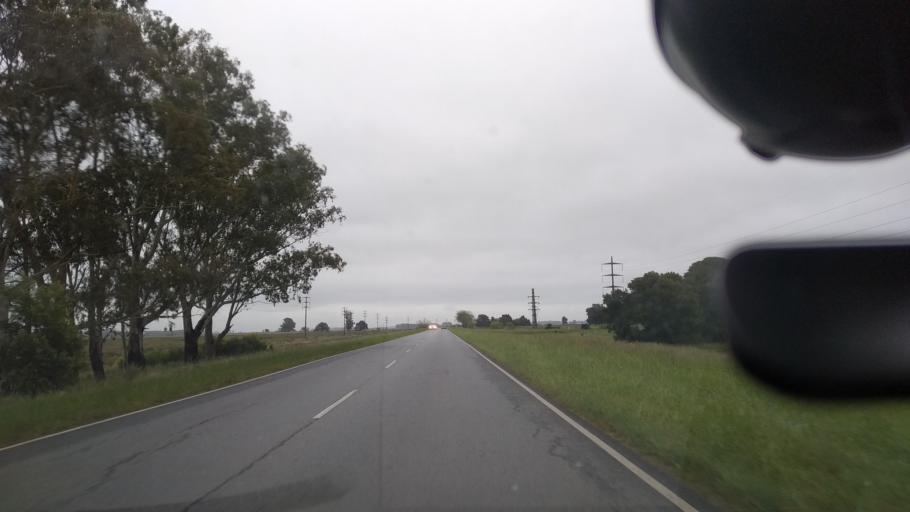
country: AR
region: Buenos Aires
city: Veronica
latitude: -35.3720
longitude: -57.3826
